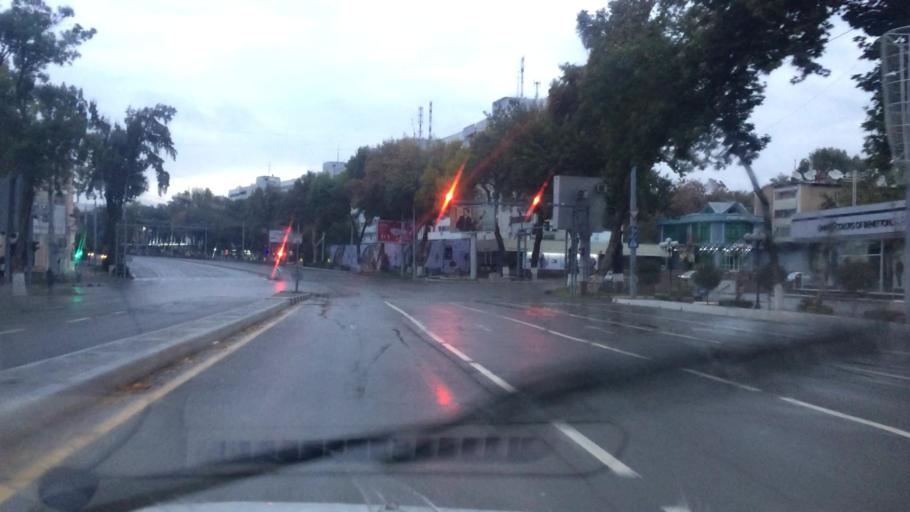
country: UZ
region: Toshkent Shahri
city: Tashkent
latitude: 41.3133
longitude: 69.2867
